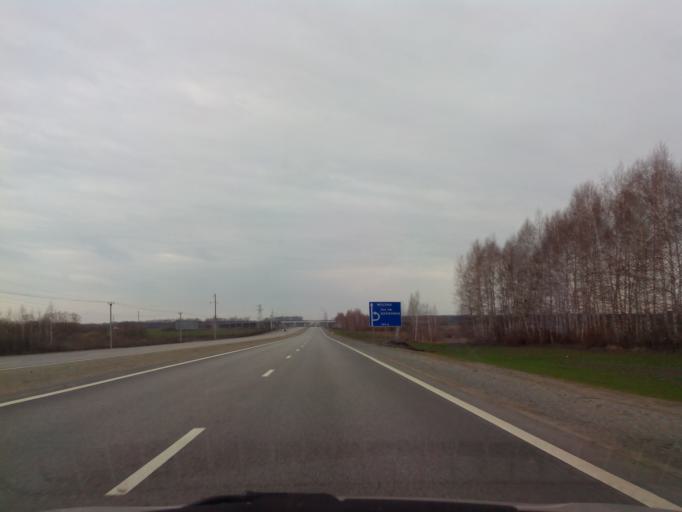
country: RU
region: Tambov
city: Zavoronezhskoye
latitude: 52.8844
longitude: 40.7223
